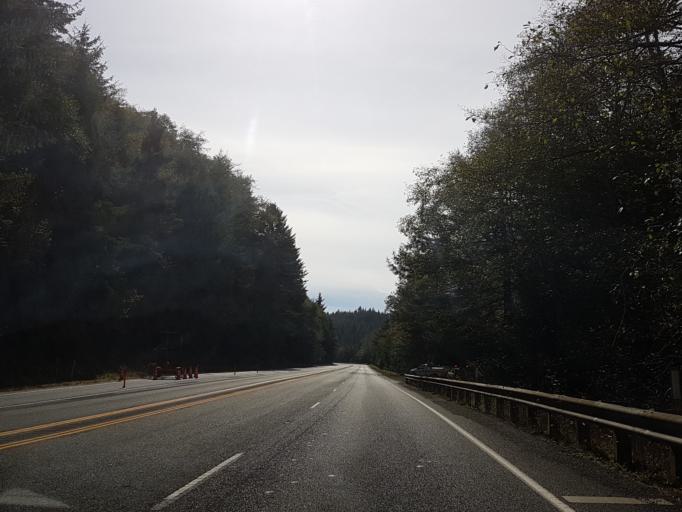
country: US
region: California
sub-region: Del Norte County
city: Bertsch-Oceanview
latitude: 41.4907
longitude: -124.0477
